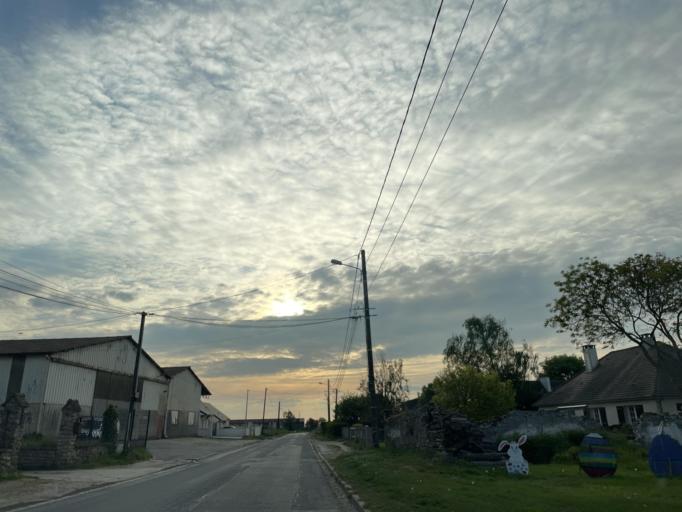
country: FR
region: Ile-de-France
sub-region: Departement de Seine-et-Marne
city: Bouleurs
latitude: 48.8916
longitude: 2.9257
